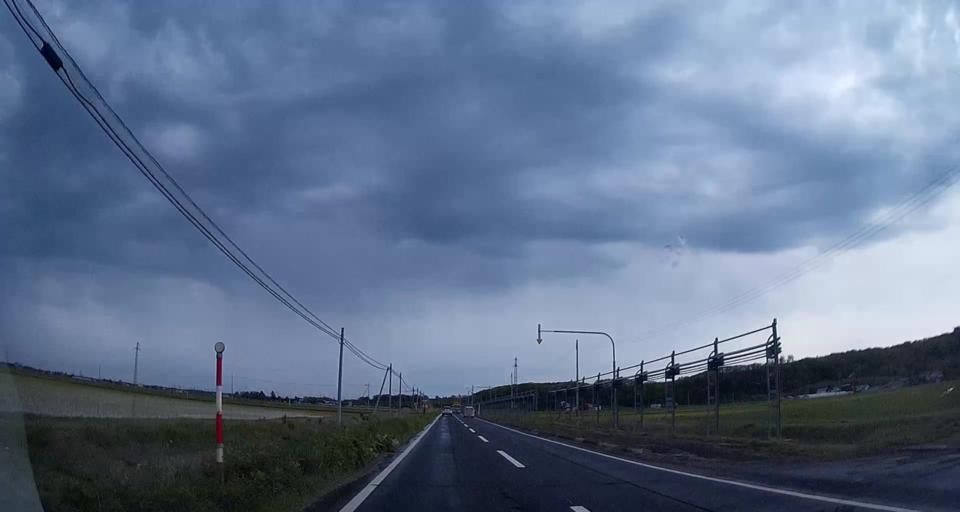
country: JP
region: Hokkaido
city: Chitose
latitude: 42.7147
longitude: 141.8601
